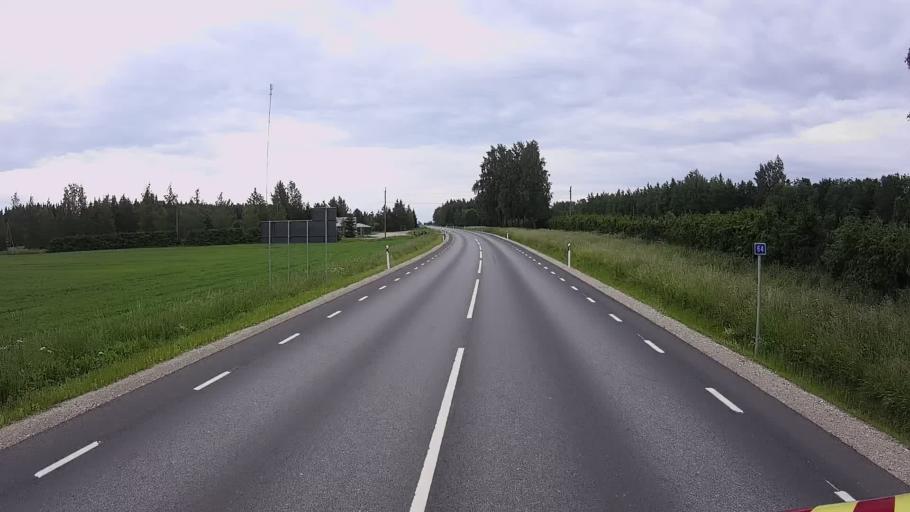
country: EE
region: Viljandimaa
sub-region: Viljandi linn
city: Viljandi
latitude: 58.2388
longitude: 25.5960
